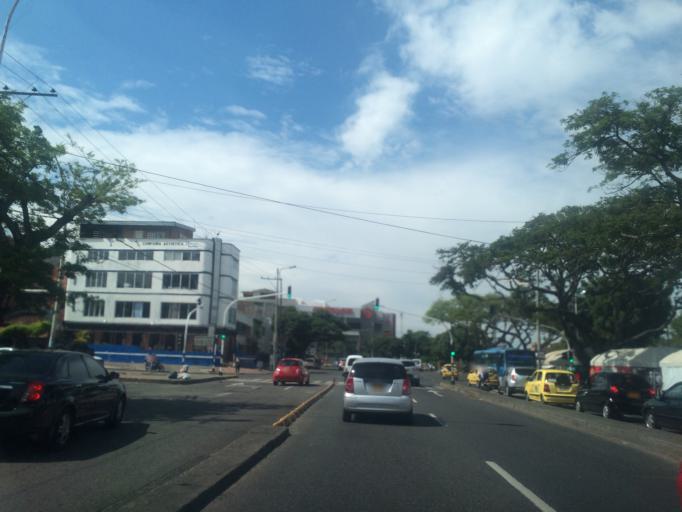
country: CO
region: Valle del Cauca
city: Cali
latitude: 3.4250
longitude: -76.5379
